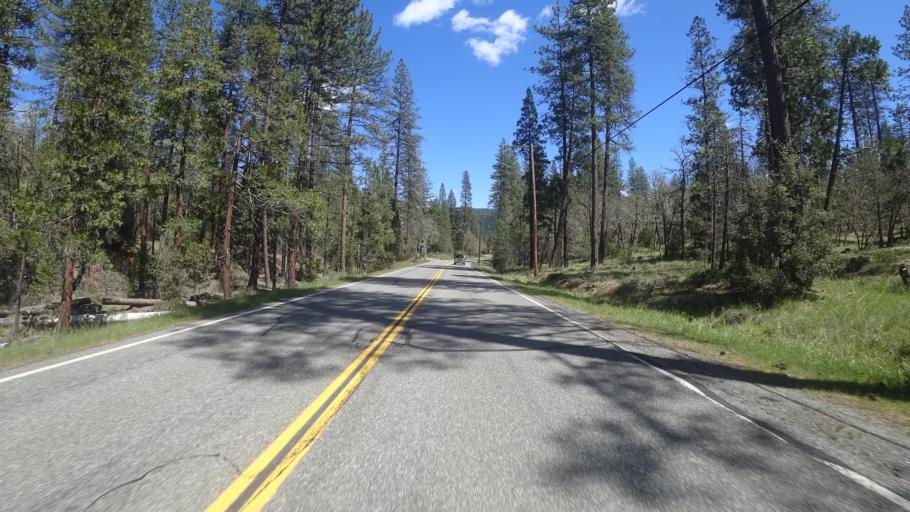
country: US
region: California
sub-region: Trinity County
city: Weaverville
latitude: 40.7520
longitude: -122.9018
